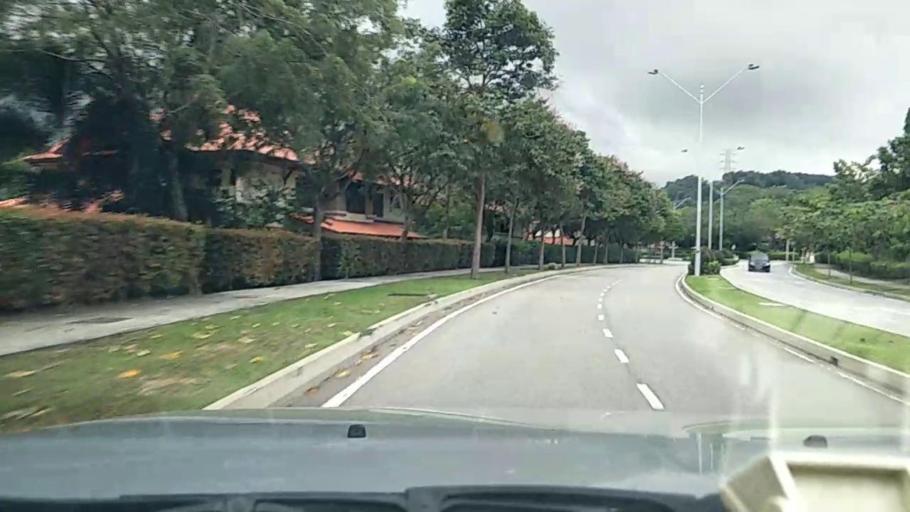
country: MY
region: Putrajaya
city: Putrajaya
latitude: 2.9327
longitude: 101.7045
